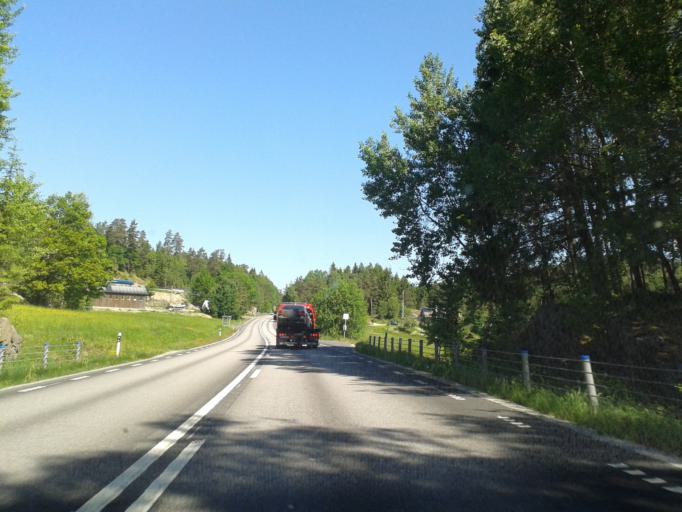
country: SE
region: Vaestra Goetaland
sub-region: Orust
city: Henan
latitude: 58.2094
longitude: 11.6917
